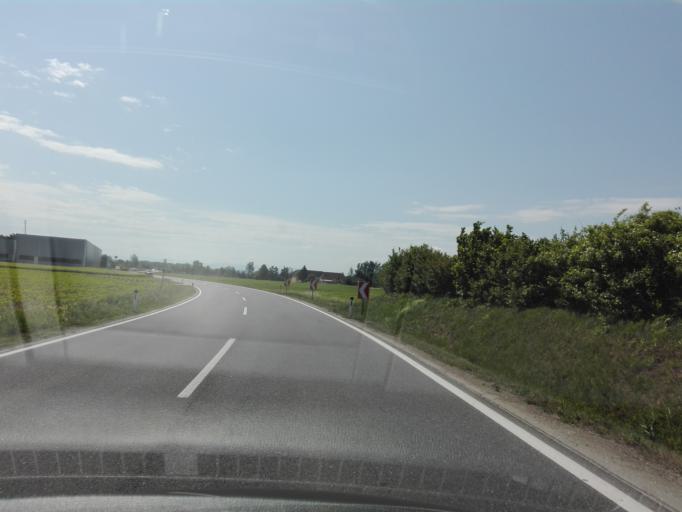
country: AT
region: Upper Austria
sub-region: Politischer Bezirk Perg
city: Perg
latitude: 48.2542
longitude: 14.5777
